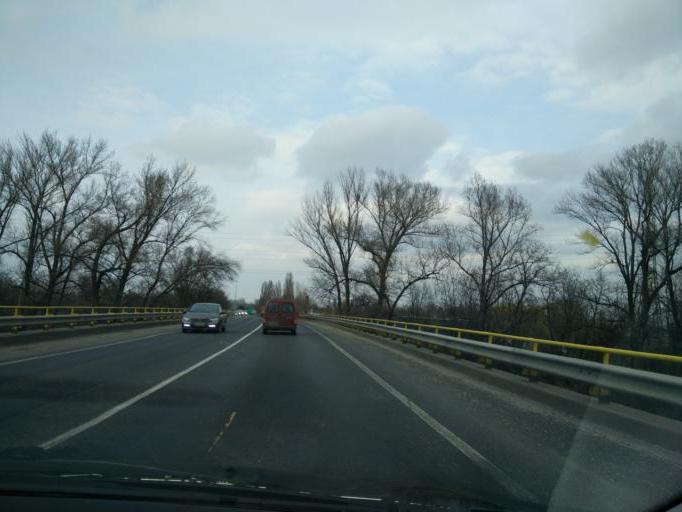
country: HU
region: Gyor-Moson-Sopron
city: Gyor
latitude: 47.7003
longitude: 17.6681
